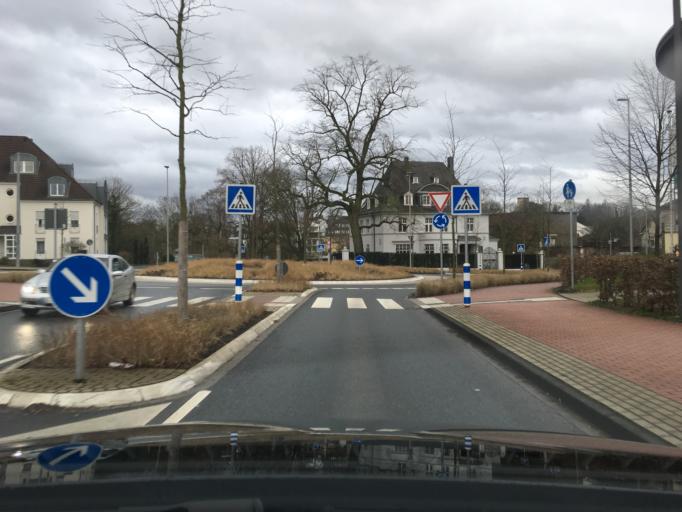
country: DE
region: North Rhine-Westphalia
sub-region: Regierungsbezirk Dusseldorf
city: Mettmann
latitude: 51.2543
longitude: 6.9827
